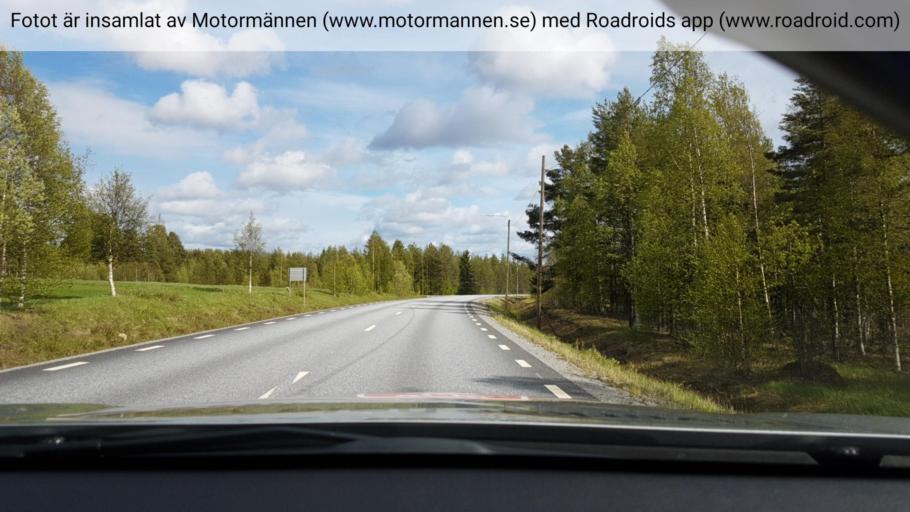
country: SE
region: Vaesterbotten
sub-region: Asele Kommun
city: Insjon
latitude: 64.1410
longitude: 18.0342
